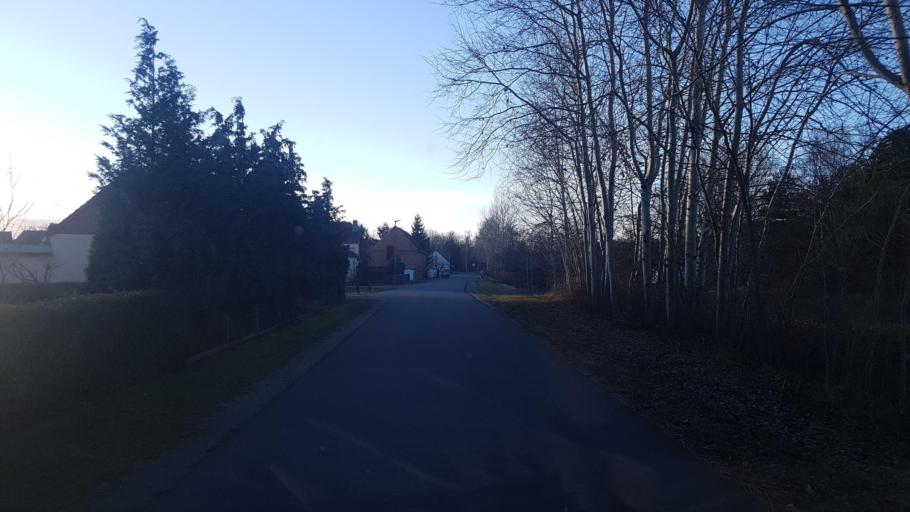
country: DE
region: Brandenburg
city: Drehnow
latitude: 51.8742
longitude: 14.3869
